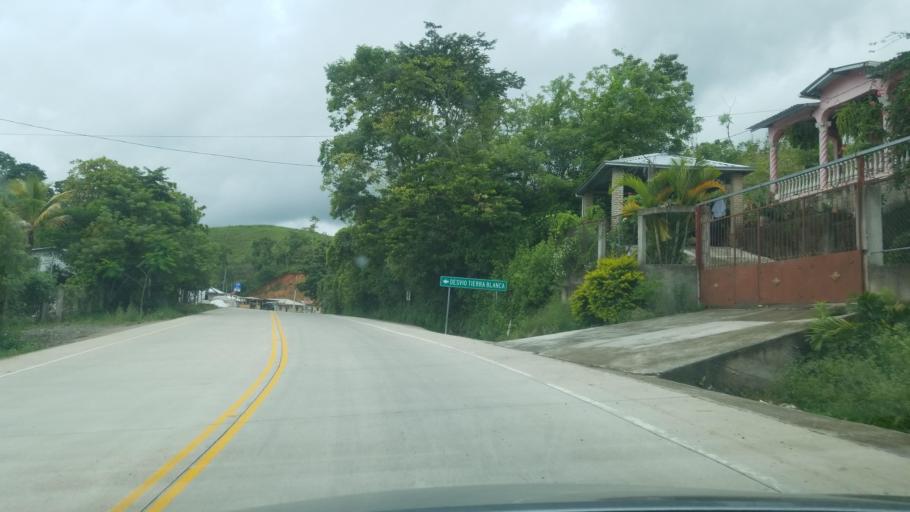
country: HN
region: Copan
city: San Jeronimo
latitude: 14.9534
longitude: -88.9074
